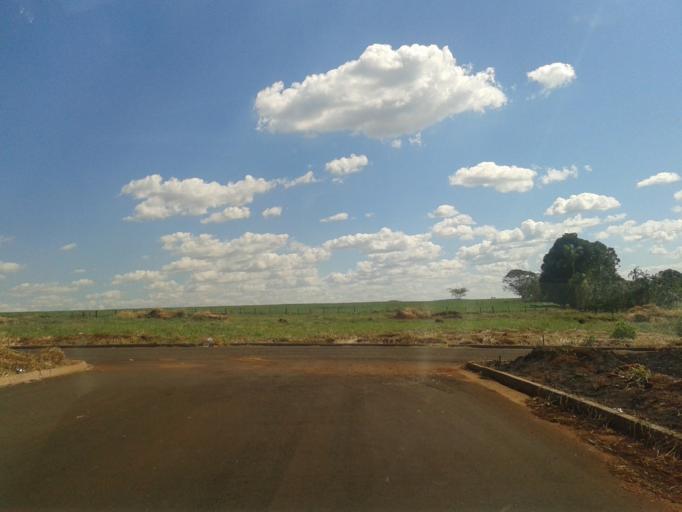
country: BR
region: Minas Gerais
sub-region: Capinopolis
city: Capinopolis
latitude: -18.6935
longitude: -49.5694
